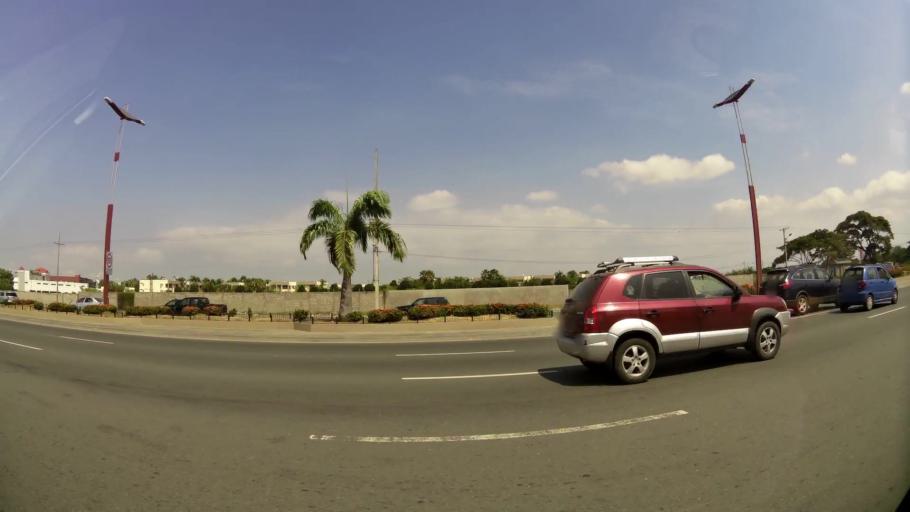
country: EC
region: Guayas
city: Eloy Alfaro
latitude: -2.1249
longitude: -79.8636
